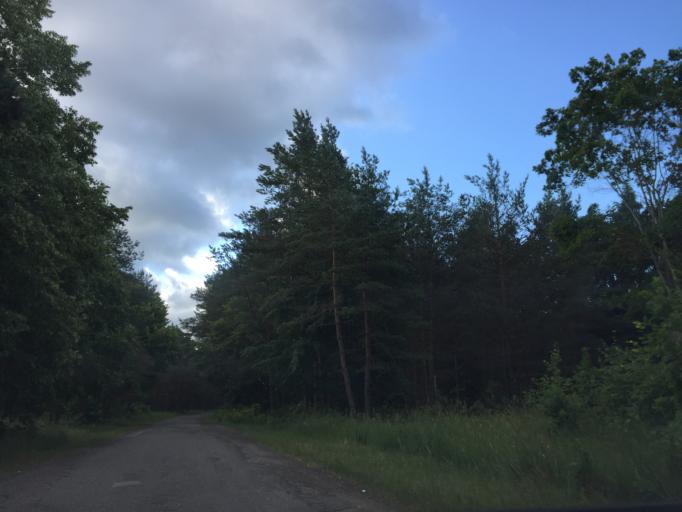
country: LV
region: Ventspils
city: Ventspils
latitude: 57.4123
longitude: 21.6117
